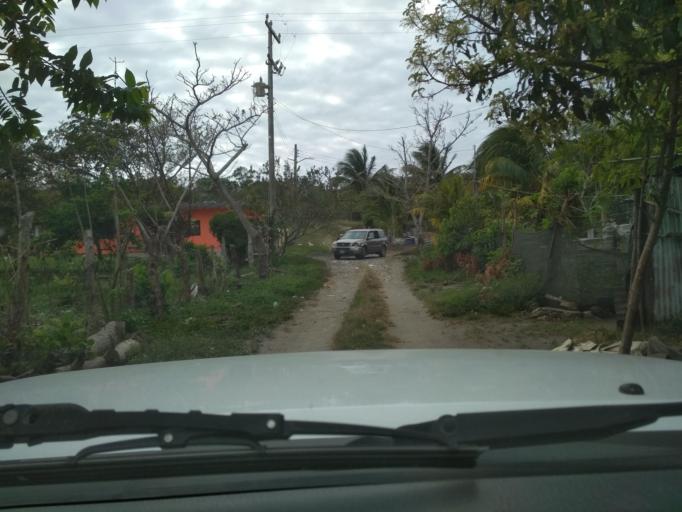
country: MX
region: Veracruz
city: Anton Lizardo
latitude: 19.0493
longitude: -95.9897
